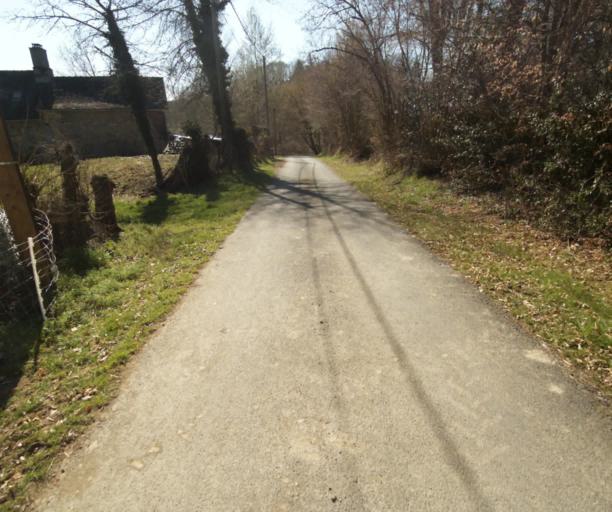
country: FR
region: Limousin
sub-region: Departement de la Correze
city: Saint-Mexant
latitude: 45.3096
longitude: 1.6227
